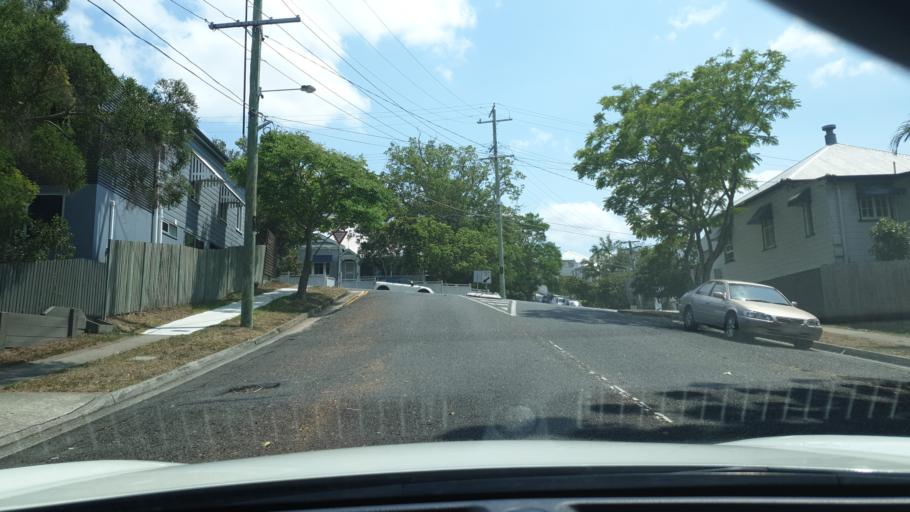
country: AU
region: Queensland
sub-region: Brisbane
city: South Brisbane
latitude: -27.4885
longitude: 153.0210
